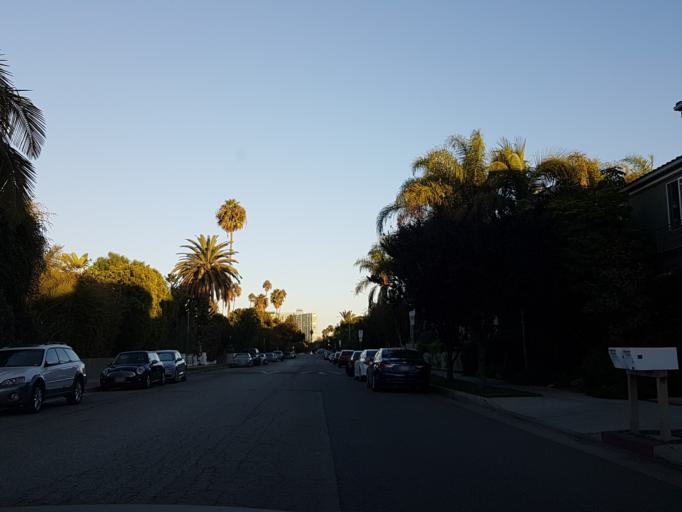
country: US
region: California
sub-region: Los Angeles County
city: Marina del Rey
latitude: 33.9873
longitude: -118.4574
